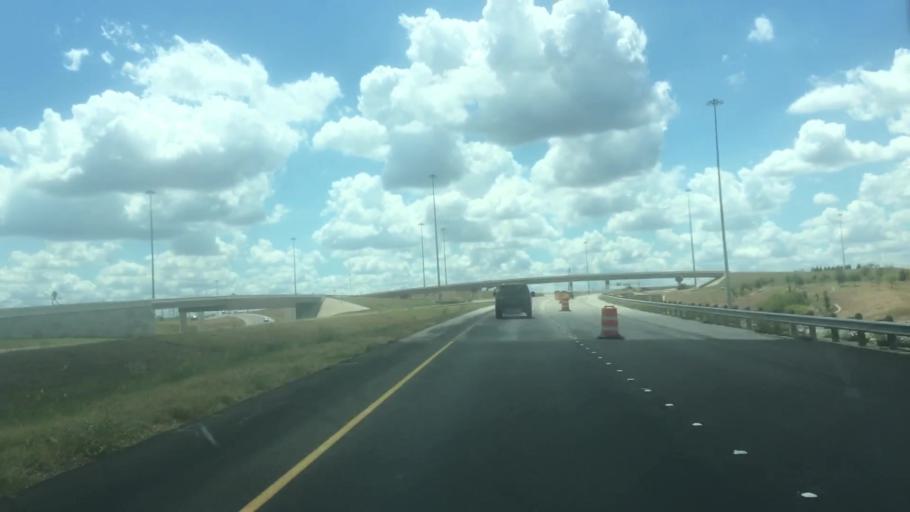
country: US
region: Texas
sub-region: Caldwell County
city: Lockhart
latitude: 29.9179
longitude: -97.6788
